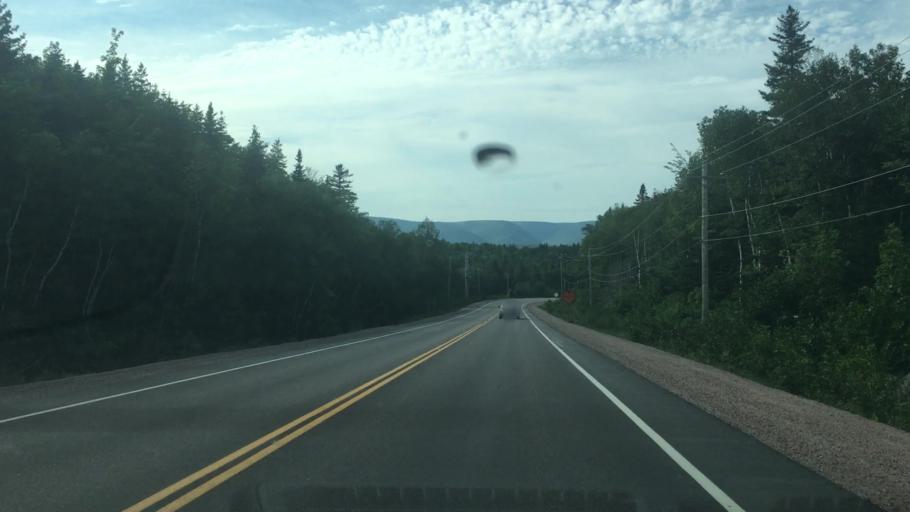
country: CA
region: Nova Scotia
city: Sydney Mines
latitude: 46.8566
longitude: -60.4599
